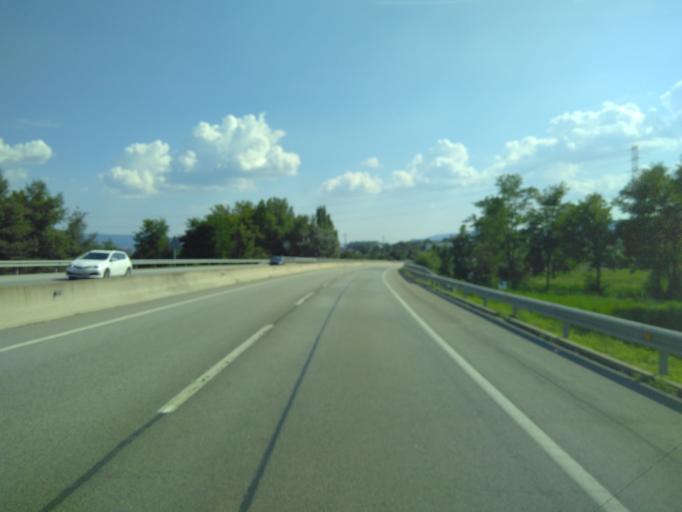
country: ES
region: Catalonia
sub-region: Provincia de Barcelona
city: Gurb
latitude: 41.9626
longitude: 2.2483
